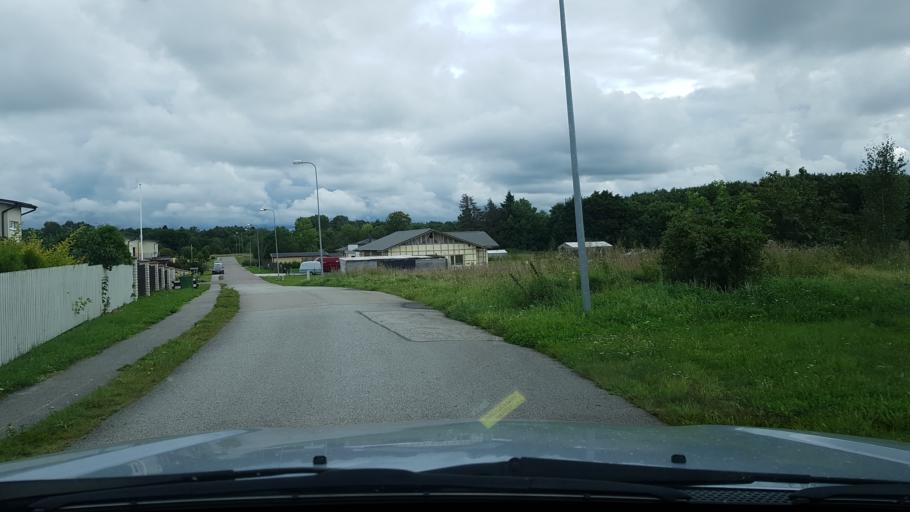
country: EE
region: Harju
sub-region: Rae vald
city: Vaida
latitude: 59.3175
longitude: 24.9436
